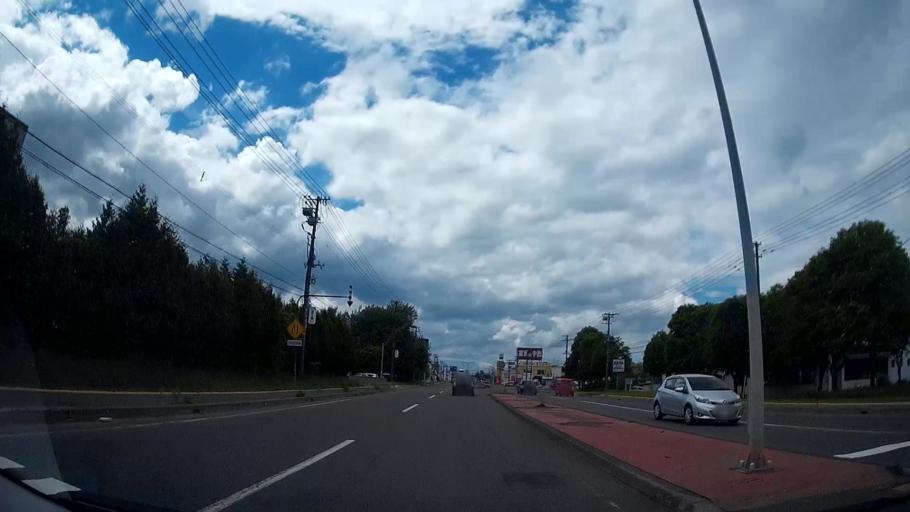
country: JP
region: Hokkaido
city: Chitose
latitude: 42.8694
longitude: 141.5894
